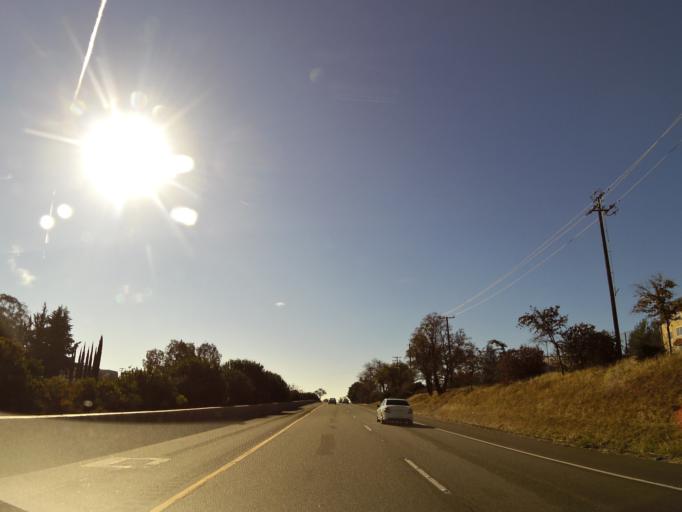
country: US
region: California
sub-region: San Luis Obispo County
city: Paso Robles
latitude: 35.6271
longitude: -120.6866
